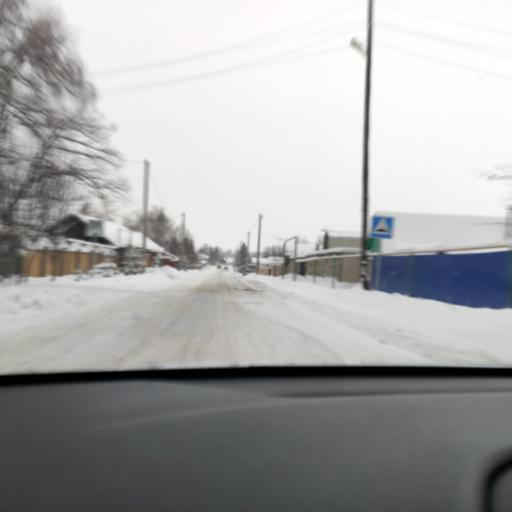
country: RU
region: Tatarstan
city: Vysokaya Gora
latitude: 55.9537
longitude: 49.1620
